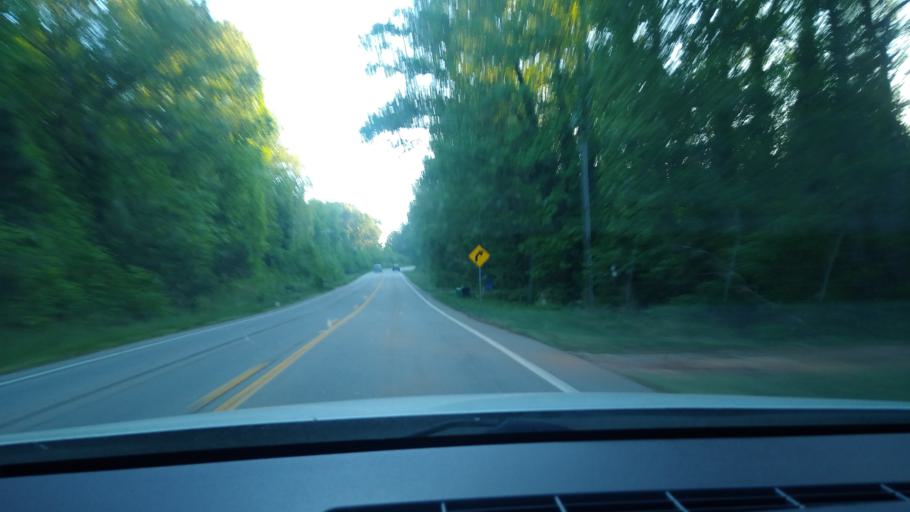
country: US
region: North Carolina
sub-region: Rockingham County
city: Reidsville
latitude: 36.3943
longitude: -79.5478
